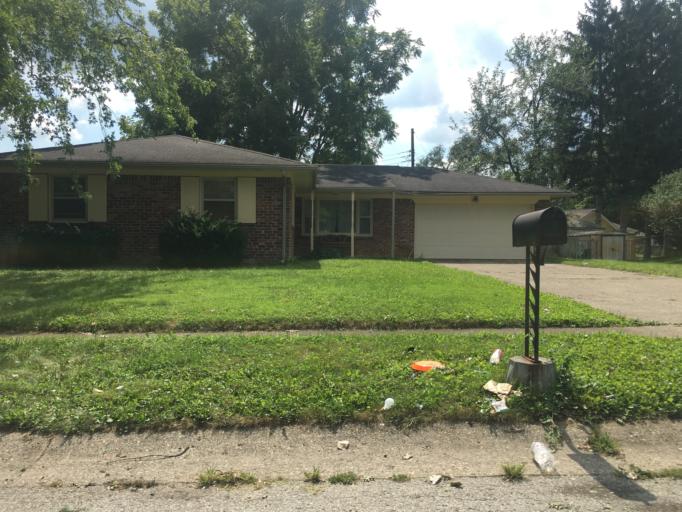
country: US
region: Indiana
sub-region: Howard County
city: Kokomo
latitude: 40.4722
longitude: -86.1033
